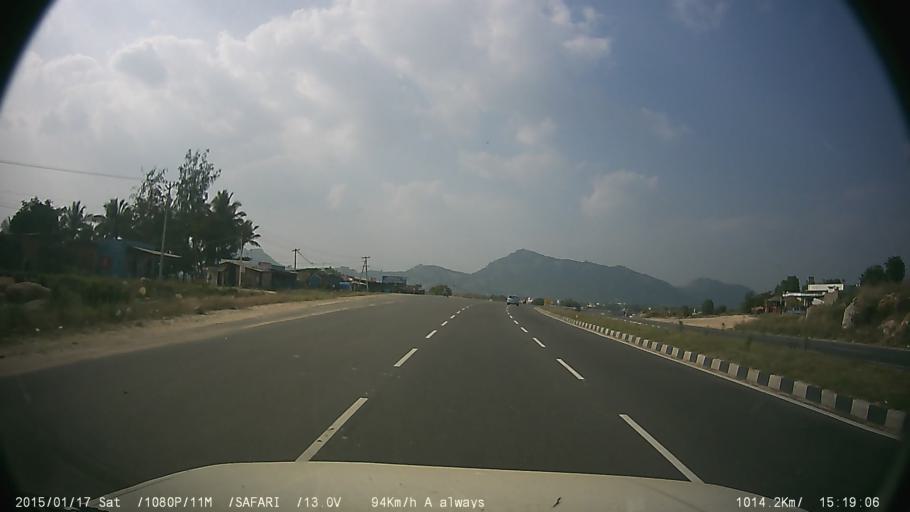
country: IN
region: Tamil Nadu
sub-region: Krishnagiri
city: Krishnagiri
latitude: 12.5921
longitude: 78.1399
